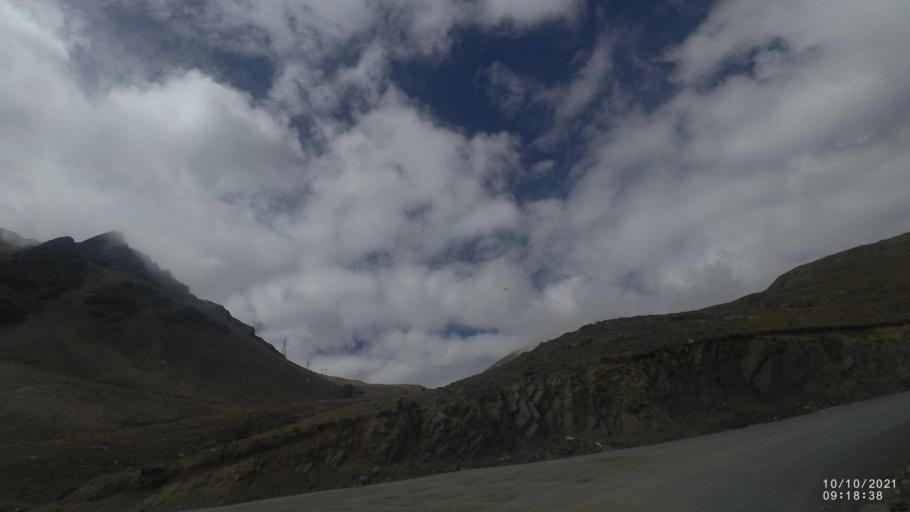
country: BO
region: La Paz
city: Quime
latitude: -17.0542
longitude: -67.2979
